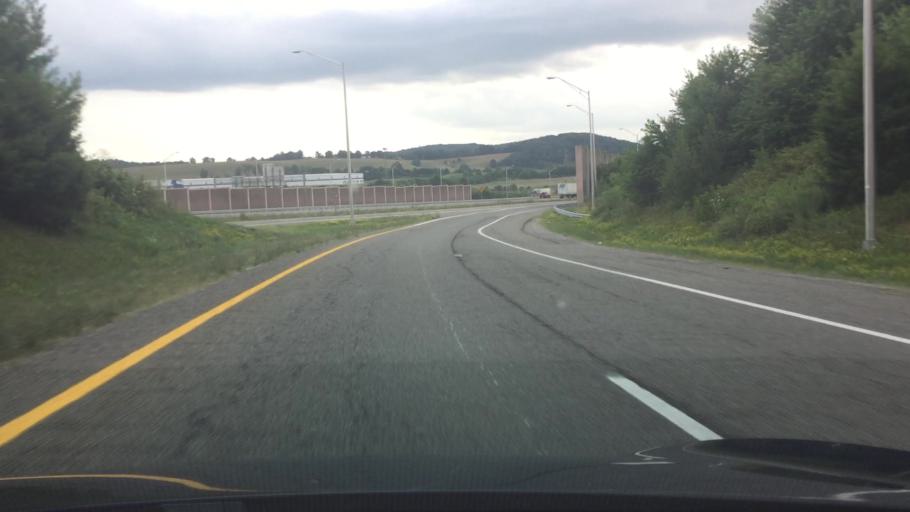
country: US
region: Virginia
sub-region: Montgomery County
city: Christiansburg
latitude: 37.1287
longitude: -80.3735
